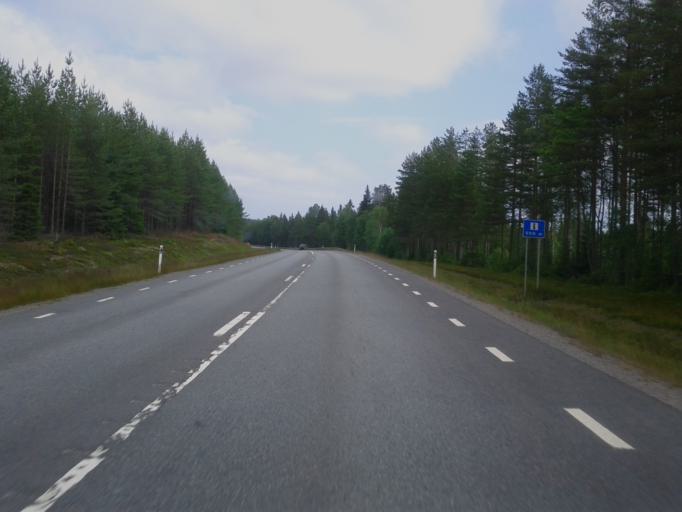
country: SE
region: Vaesterbotten
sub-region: Skelleftea Kommun
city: Burea
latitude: 64.3485
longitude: 21.2912
